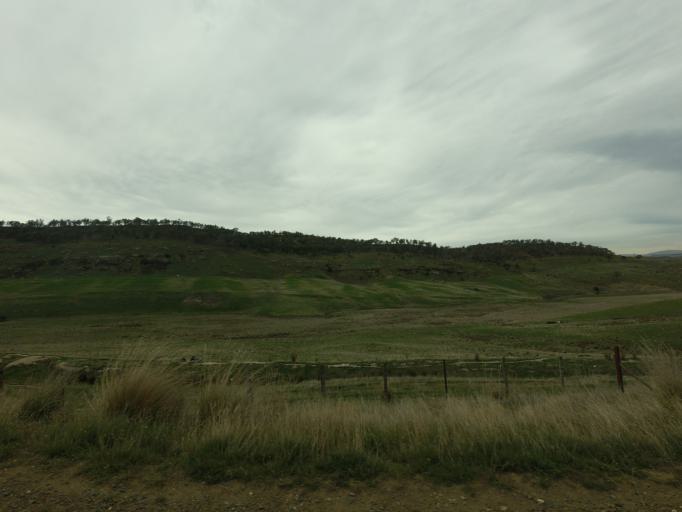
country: AU
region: Tasmania
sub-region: Derwent Valley
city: New Norfolk
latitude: -42.3993
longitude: 146.9188
